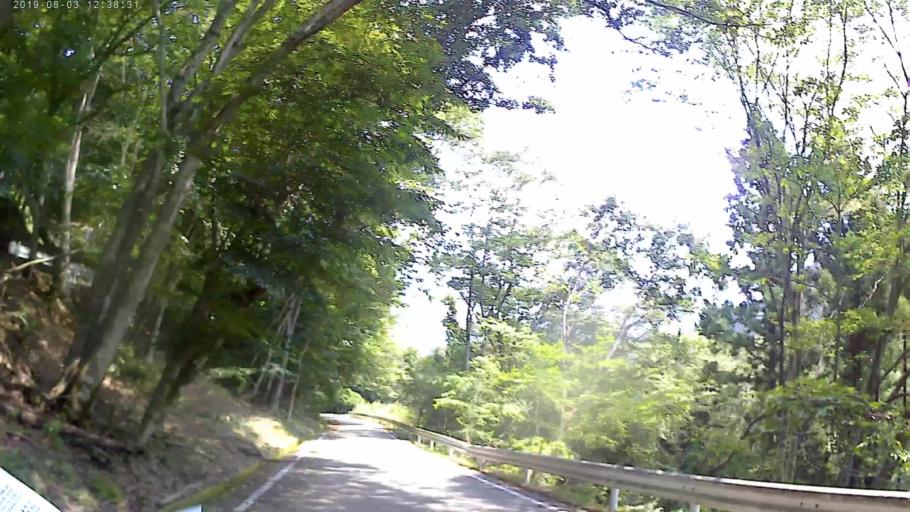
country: JP
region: Yamanashi
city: Enzan
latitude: 35.6067
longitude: 138.7934
